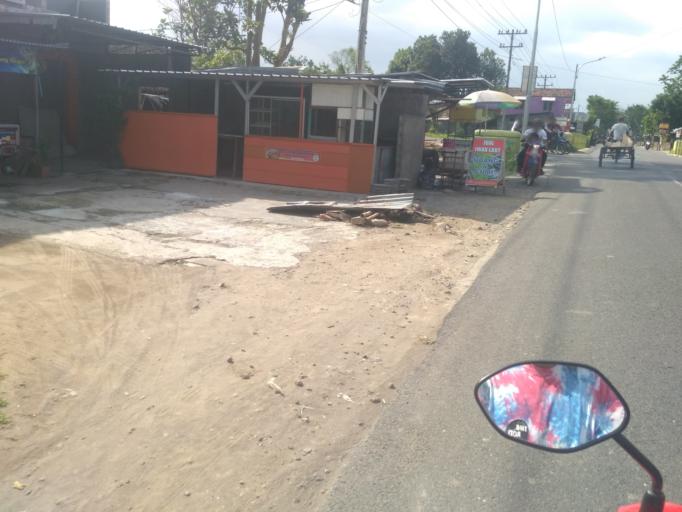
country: ID
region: Daerah Istimewa Yogyakarta
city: Godean
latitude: -7.7486
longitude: 110.3210
